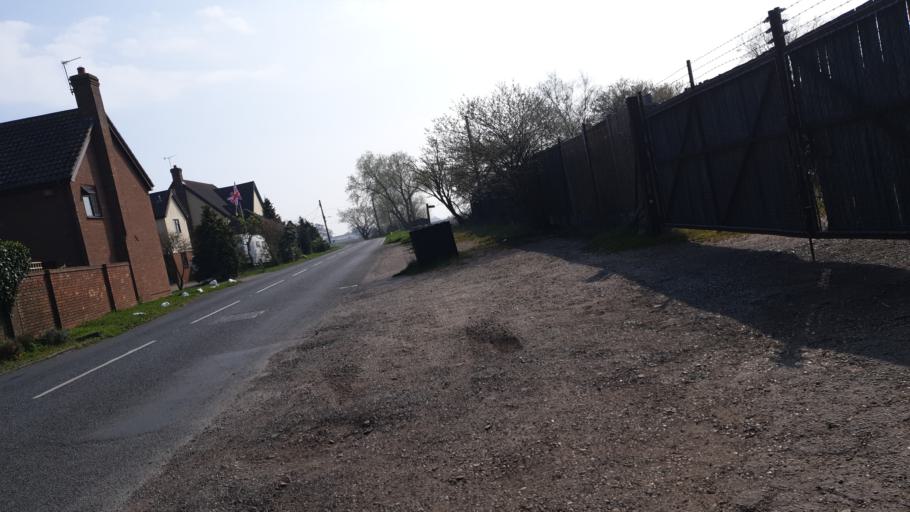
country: GB
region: England
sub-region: Essex
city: Mistley
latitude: 51.9108
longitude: 1.1429
